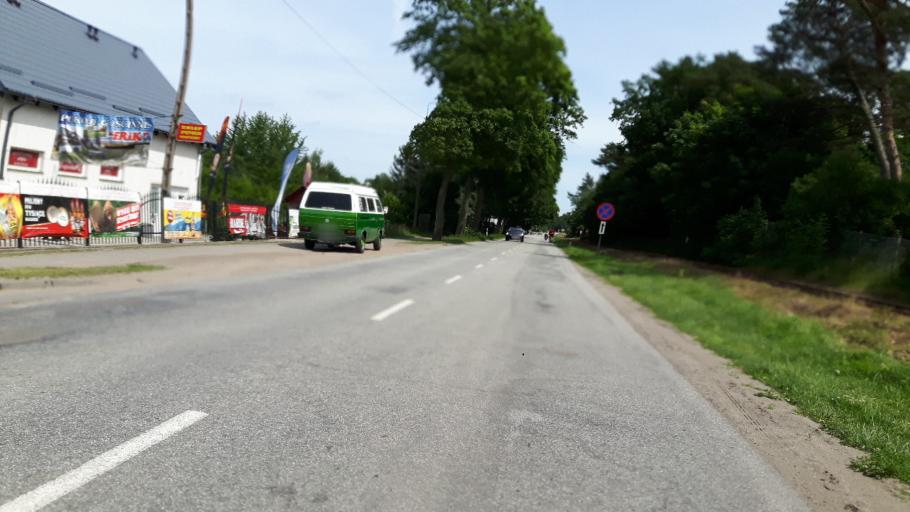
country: PL
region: Pomeranian Voivodeship
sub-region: Powiat nowodworski
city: Stegna
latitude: 54.3332
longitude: 19.0470
